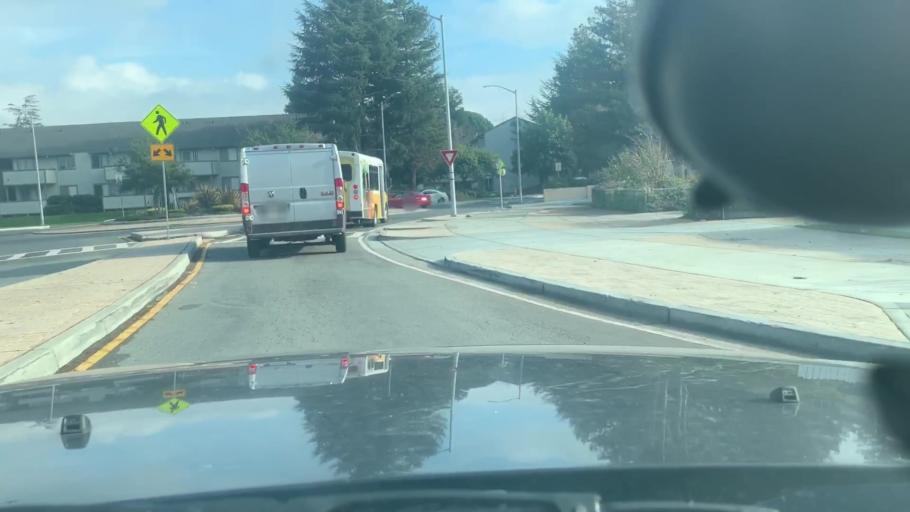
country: US
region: California
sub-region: Alameda County
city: Fremont
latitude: 37.5427
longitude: -121.9857
